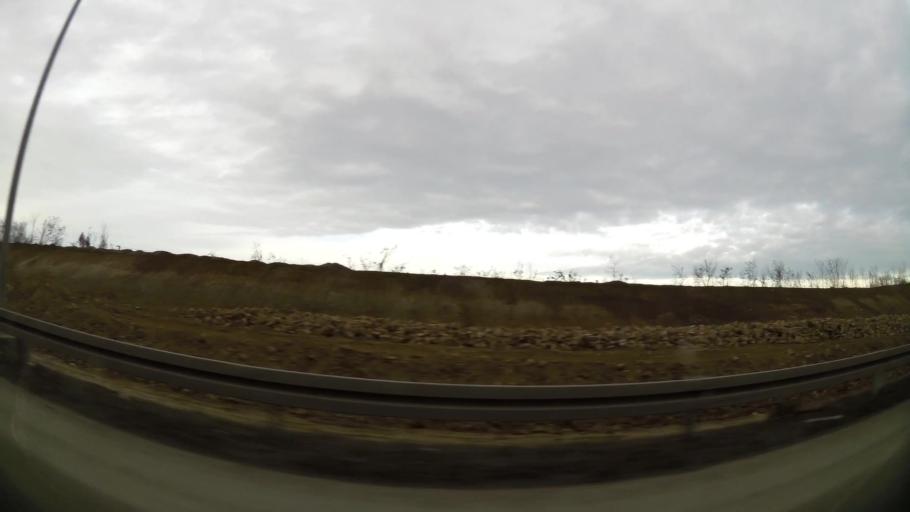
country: RS
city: Ostruznica
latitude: 44.7264
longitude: 20.3541
